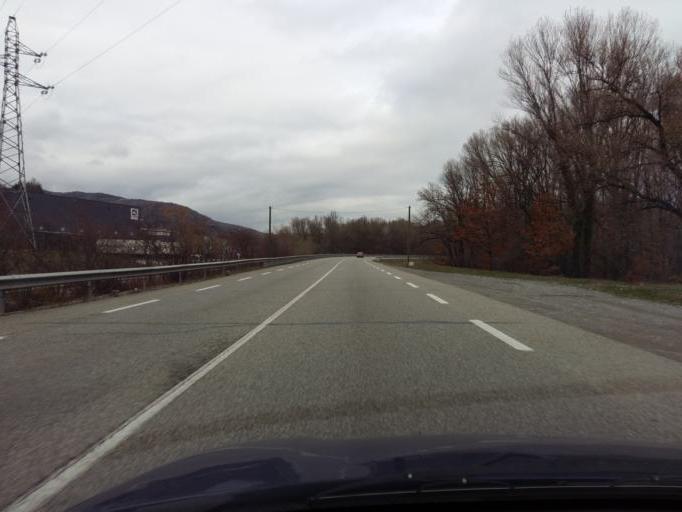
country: FR
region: Rhone-Alpes
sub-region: Departement de l'Ardeche
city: Beauchastel
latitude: 44.8098
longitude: 4.7970
